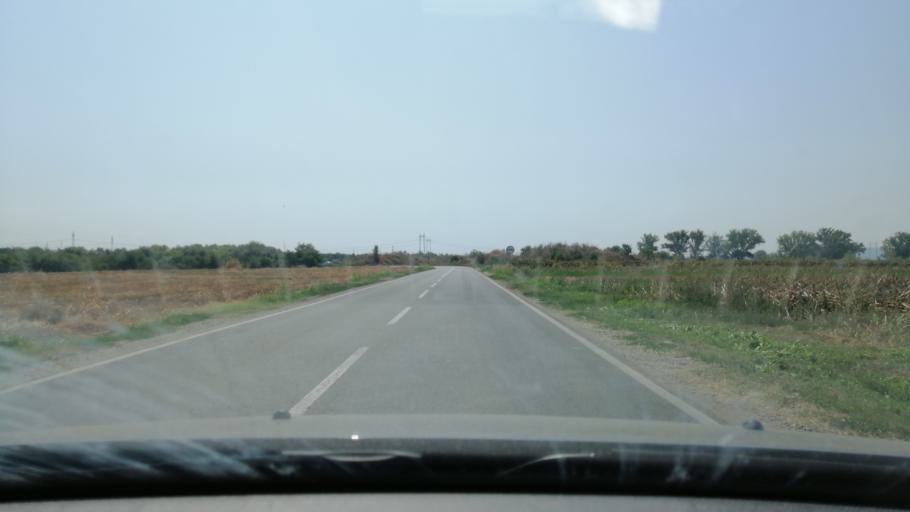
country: RS
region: Autonomna Pokrajina Vojvodina
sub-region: Juznobanatski Okrug
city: Pancevo
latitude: 44.7944
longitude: 20.7201
